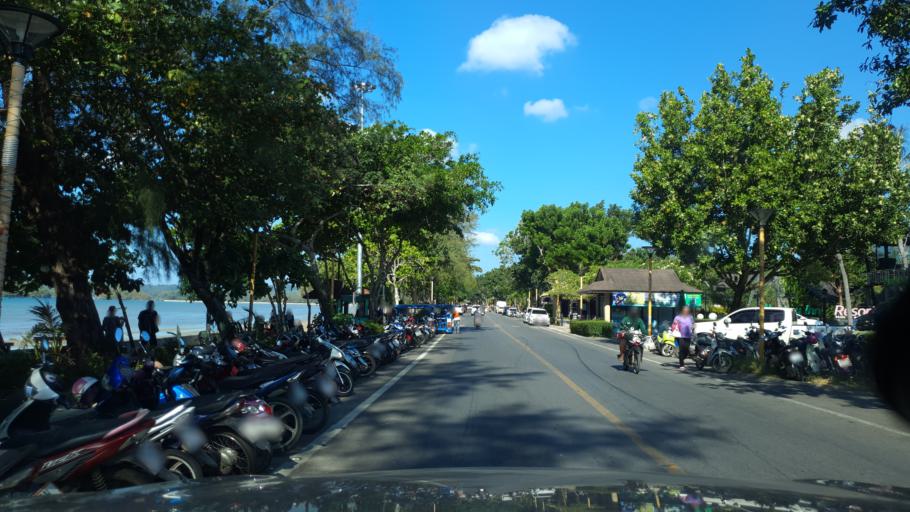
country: TH
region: Phangnga
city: Ban Ao Nang
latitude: 8.0396
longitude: 98.8152
